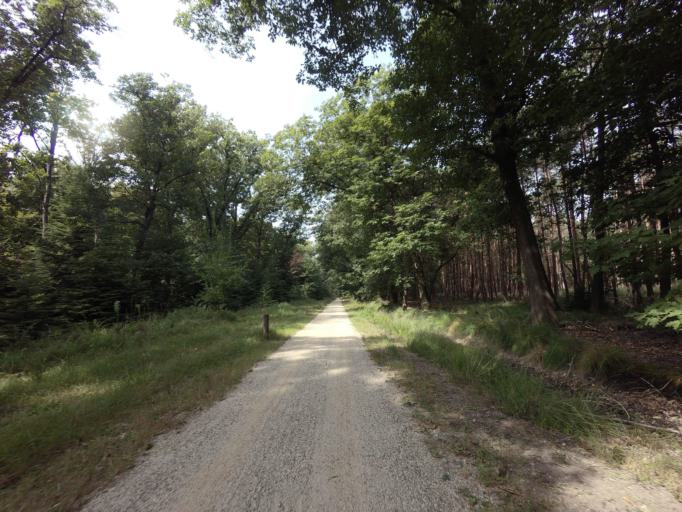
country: NL
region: North Brabant
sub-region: Gemeente Mill en Sint Hubert
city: Wilbertoord
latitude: 51.5369
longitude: 5.7913
